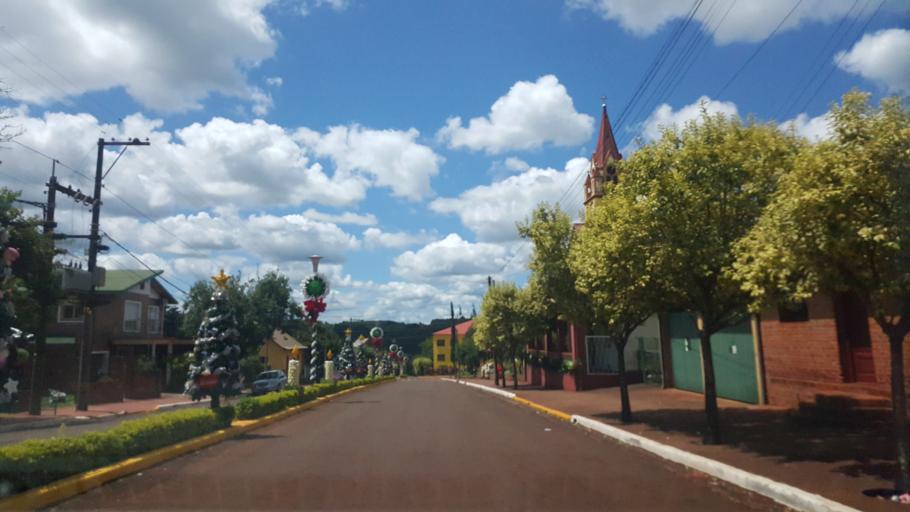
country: AR
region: Misiones
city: Capiovi
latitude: -26.9279
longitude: -55.0577
